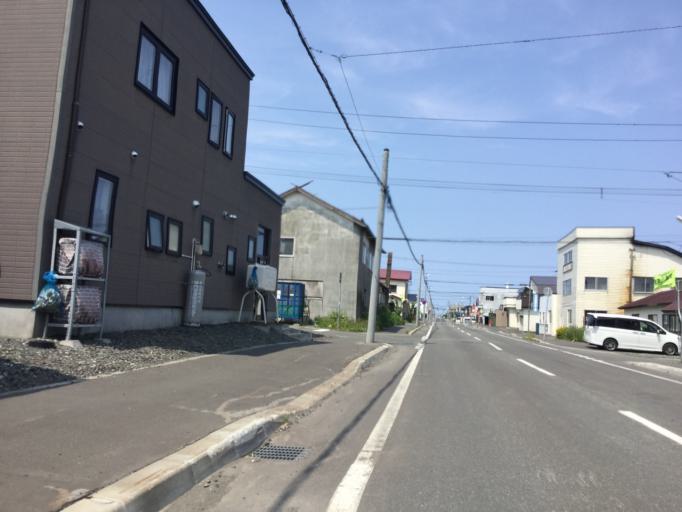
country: JP
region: Hokkaido
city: Wakkanai
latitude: 45.3882
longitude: 141.7012
